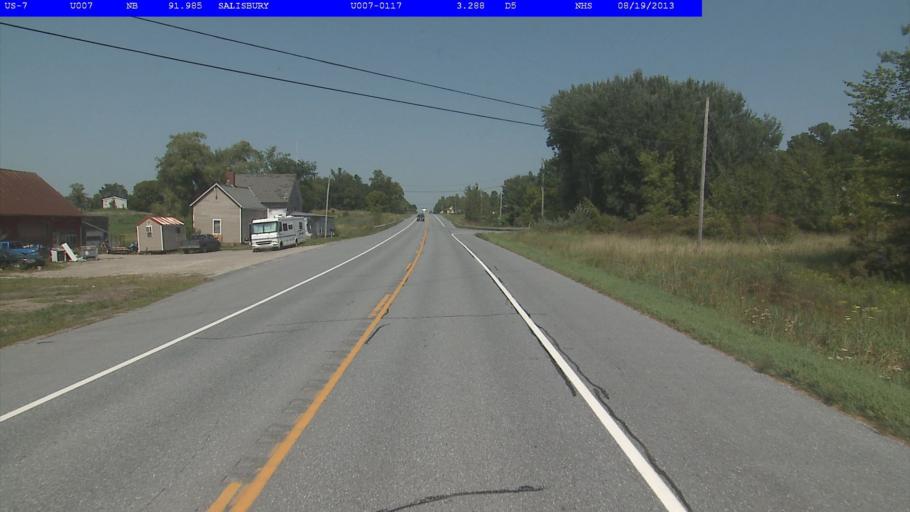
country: US
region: Vermont
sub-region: Addison County
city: Middlebury (village)
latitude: 43.9391
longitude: -73.1098
